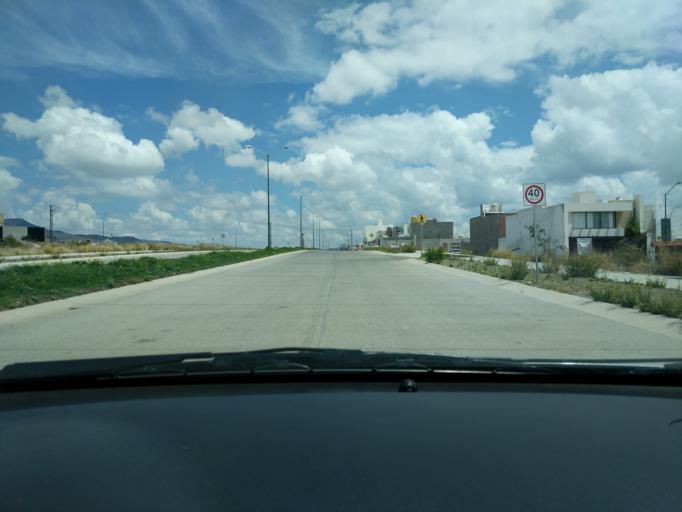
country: MX
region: San Luis Potosi
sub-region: Mexquitic de Carmona
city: Guadalupe Victoria
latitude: 22.1578
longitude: -101.0539
